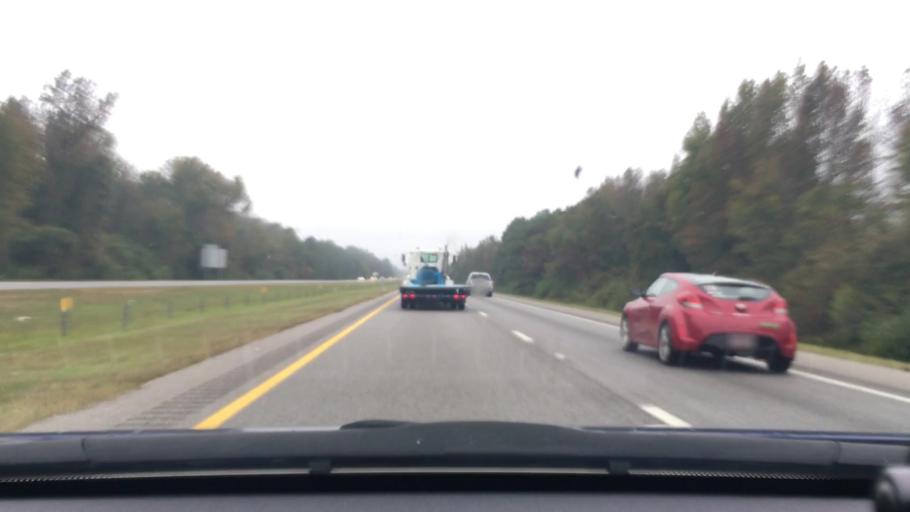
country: US
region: South Carolina
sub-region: Lee County
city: Bishopville
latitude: 34.1876
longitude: -80.2319
